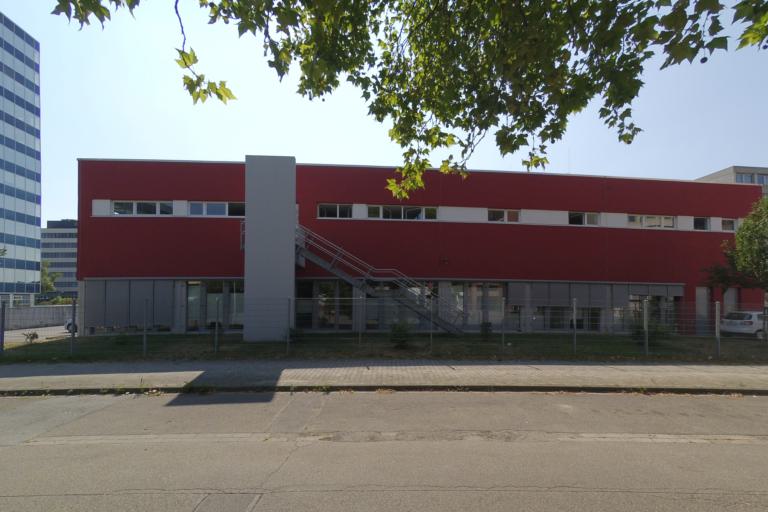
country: DE
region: Baden-Wuerttemberg
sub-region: Karlsruhe Region
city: Mannheim
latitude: 49.4996
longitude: 8.4994
